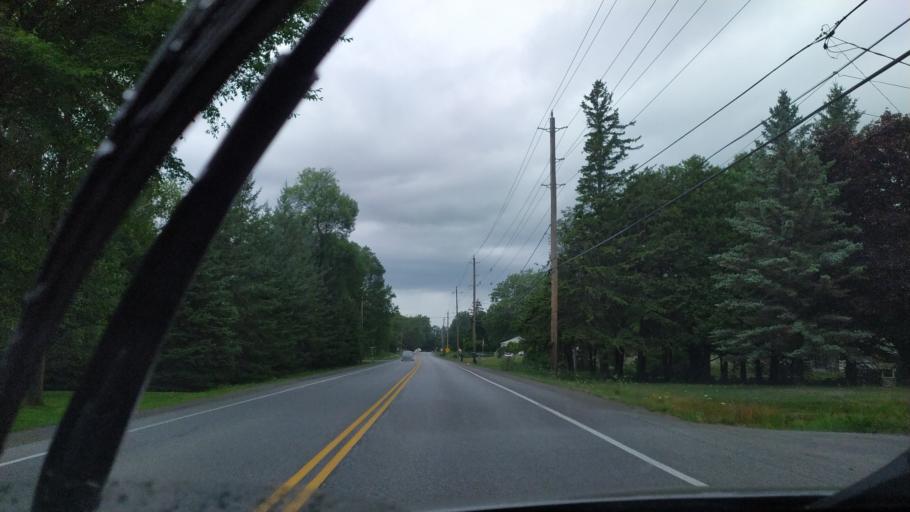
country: CA
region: Ontario
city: Quinte West
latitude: 44.0524
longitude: -77.5904
